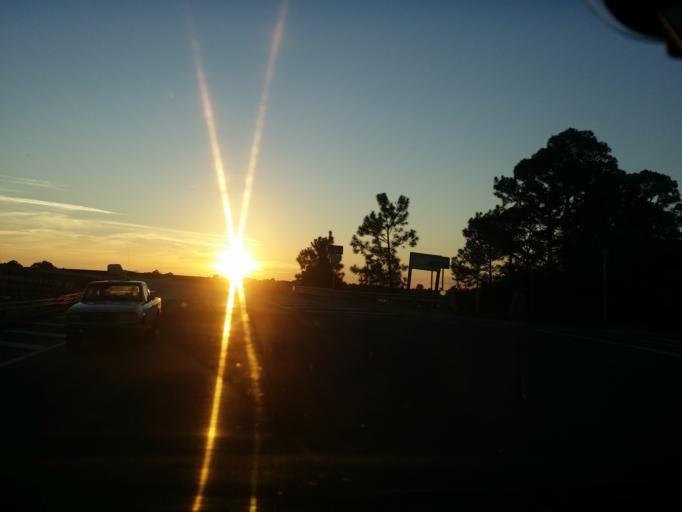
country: US
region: Florida
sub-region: Franklin County
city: Carrabelle
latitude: 29.8529
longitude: -84.6745
